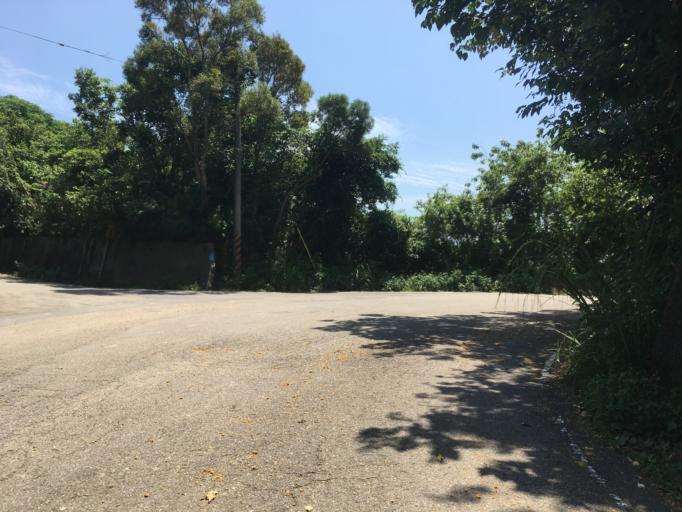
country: TW
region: Taiwan
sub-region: Hsinchu
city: Hsinchu
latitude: 24.7347
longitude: 120.9880
